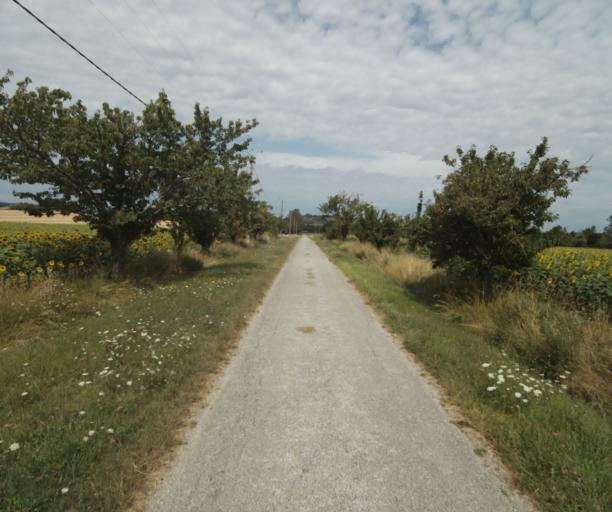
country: FR
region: Midi-Pyrenees
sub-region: Departement de la Haute-Garonne
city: Saint-Felix-Lauragais
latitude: 43.4202
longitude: 1.9132
